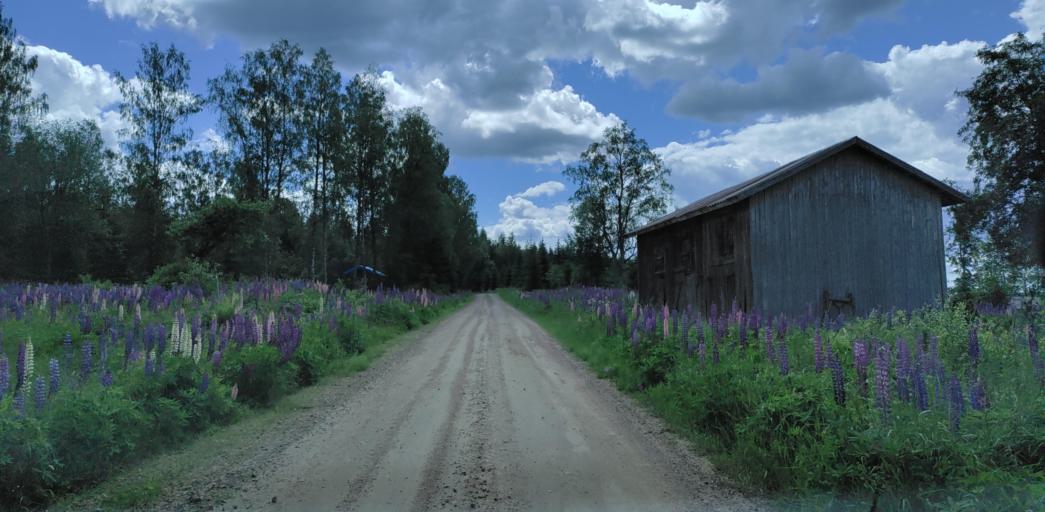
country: SE
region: Vaermland
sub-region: Hagfors Kommun
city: Ekshaerad
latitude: 60.0819
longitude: 13.3140
